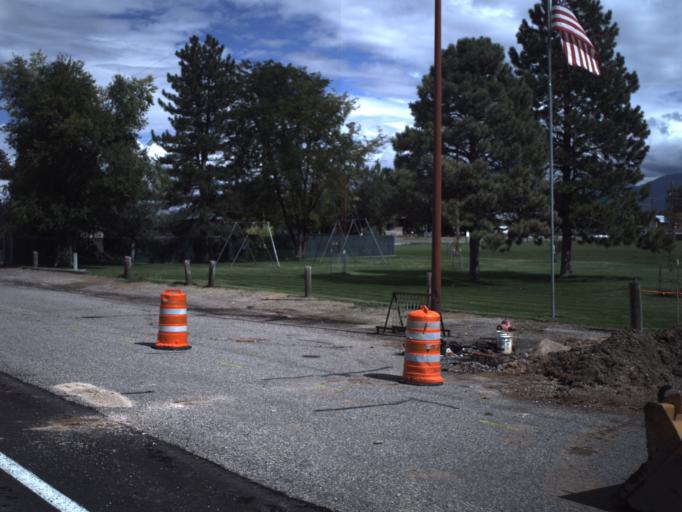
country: US
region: Utah
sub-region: Millard County
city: Fillmore
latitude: 38.8850
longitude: -112.4105
